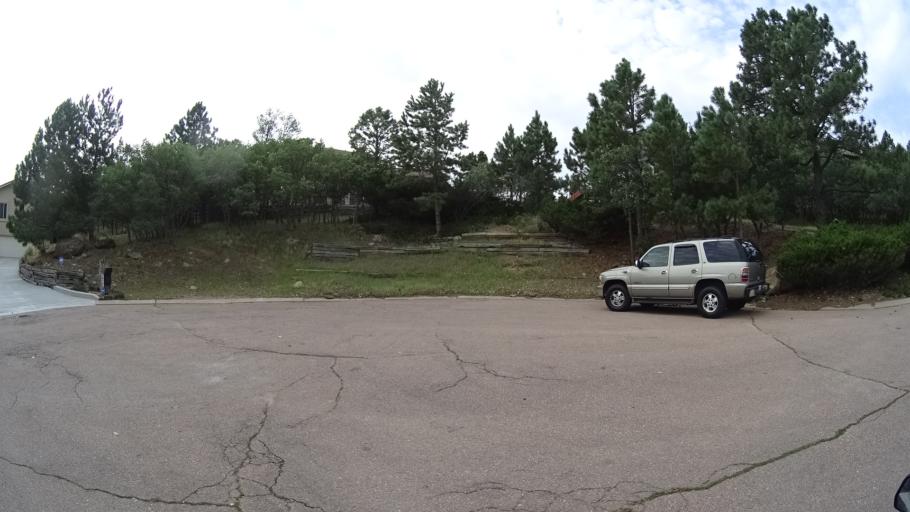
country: US
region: Colorado
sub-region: El Paso County
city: Air Force Academy
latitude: 38.9286
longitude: -104.8502
